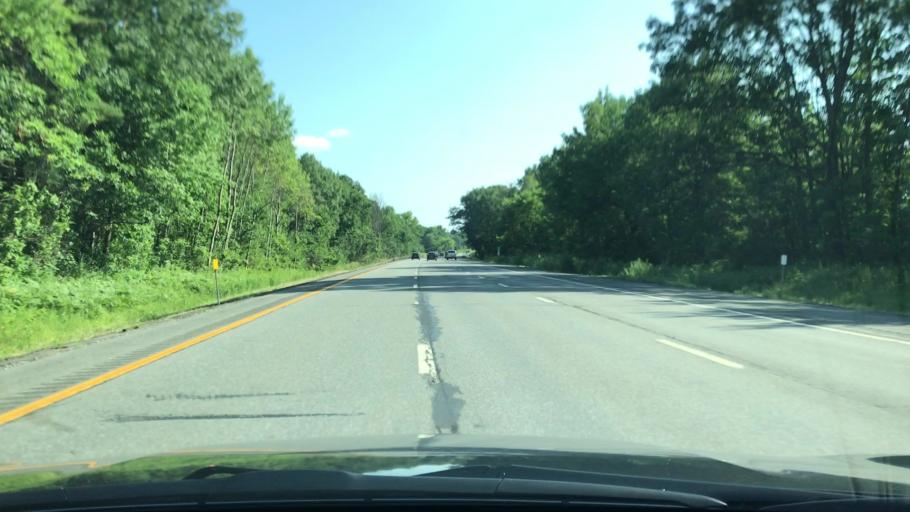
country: US
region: New York
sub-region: Warren County
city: West Glens Falls
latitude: 43.2099
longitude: -73.6943
